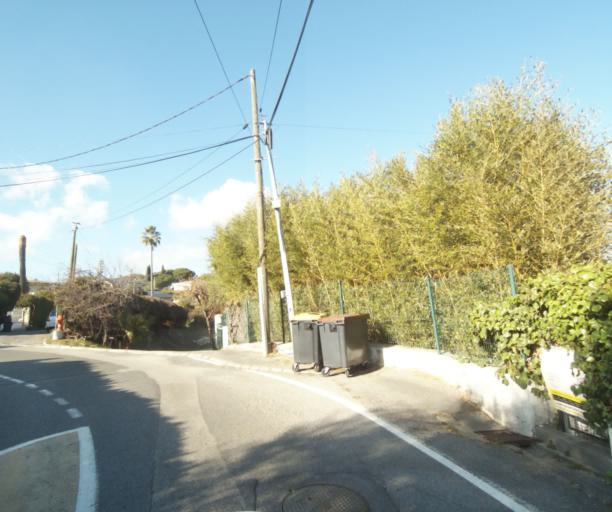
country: FR
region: Provence-Alpes-Cote d'Azur
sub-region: Departement des Alpes-Maritimes
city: Biot
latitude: 43.6041
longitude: 7.1078
